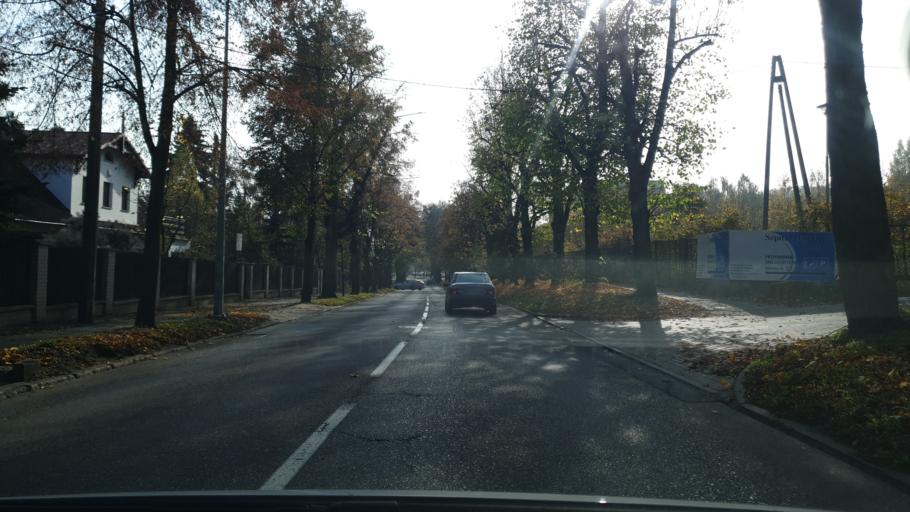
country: PL
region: Pomeranian Voivodeship
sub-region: Sopot
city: Sopot
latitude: 54.3969
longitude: 18.5646
